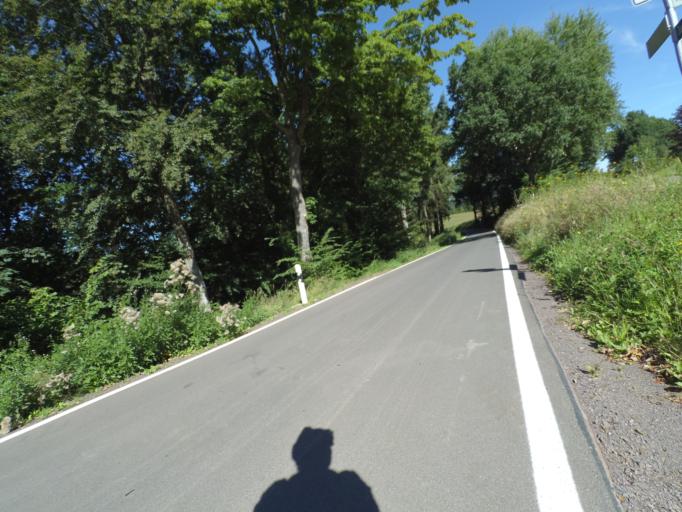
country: DE
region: Rheinland-Pfalz
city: Plein
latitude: 50.0338
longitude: 6.8816
